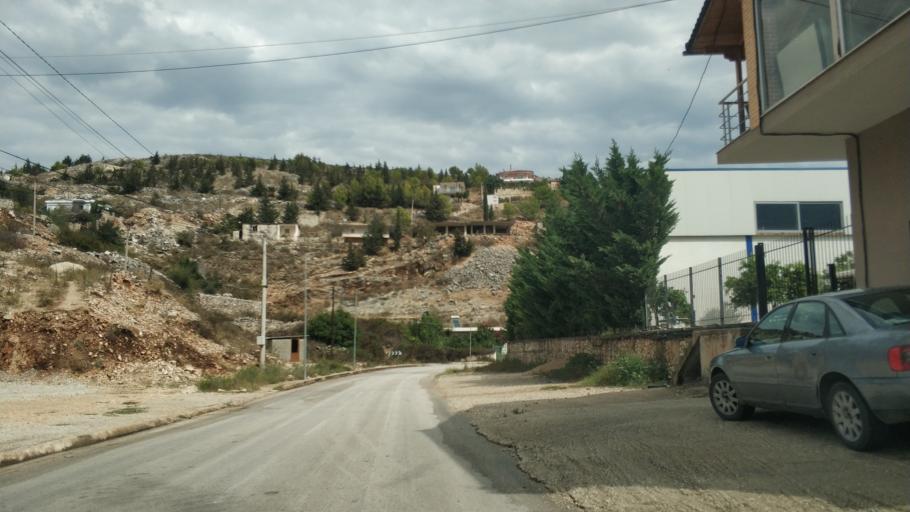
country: AL
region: Vlore
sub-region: Rrethi i Sarandes
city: Sarande
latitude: 39.8495
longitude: 20.0273
